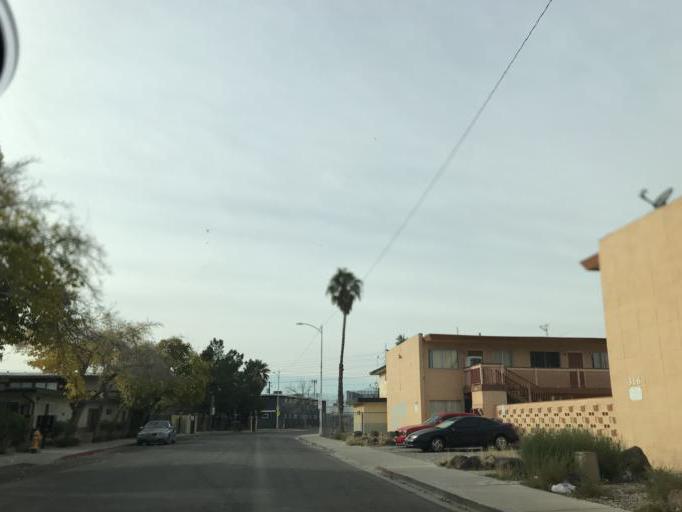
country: US
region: Nevada
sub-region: Clark County
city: Las Vegas
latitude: 36.1457
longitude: -115.1611
